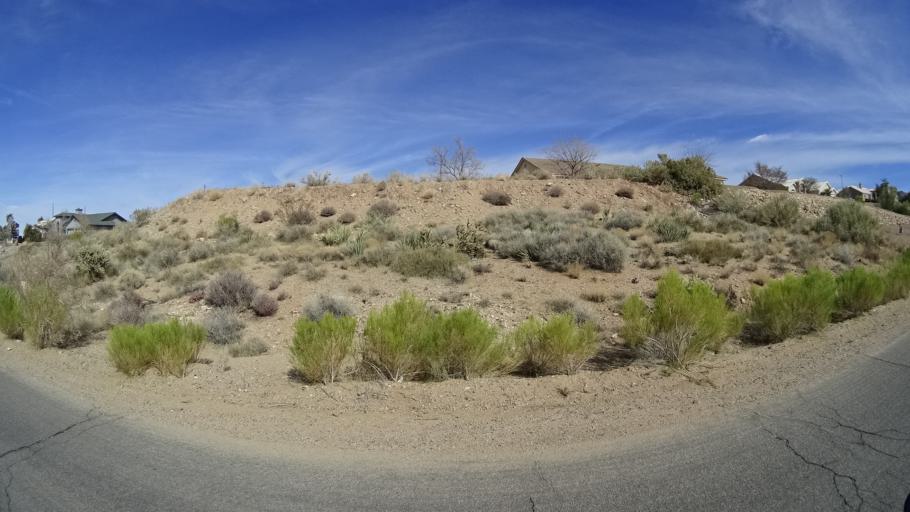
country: US
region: Arizona
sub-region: Mohave County
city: Kingman
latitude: 35.1794
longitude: -113.9890
